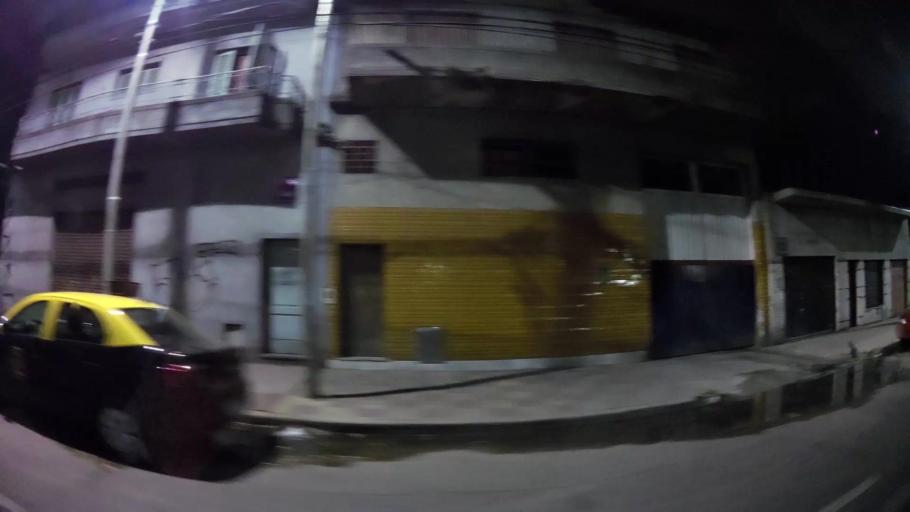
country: AR
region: Buenos Aires
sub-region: Partido de Lanus
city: Lanus
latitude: -34.7194
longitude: -58.3354
